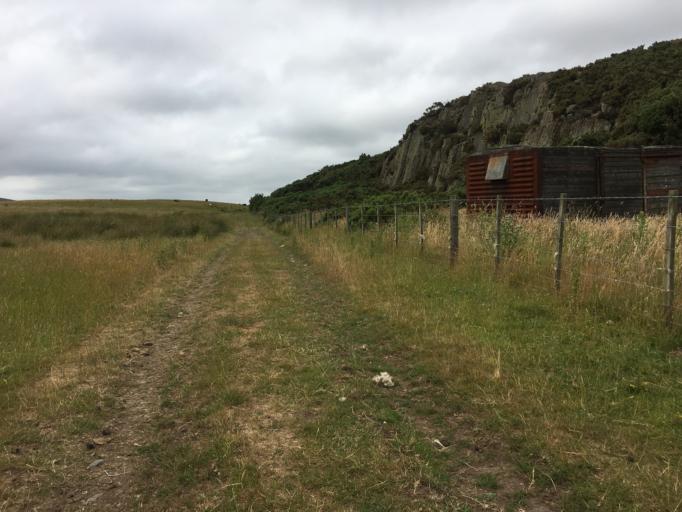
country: GB
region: England
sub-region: Northumberland
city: Belford
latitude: 55.6131
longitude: -1.8918
